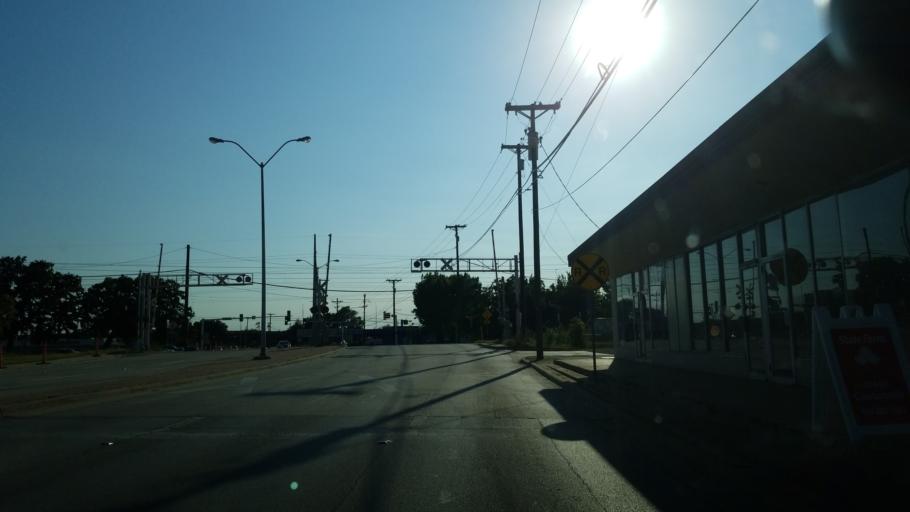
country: US
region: Texas
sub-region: Dallas County
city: Farmers Branch
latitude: 32.9240
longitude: -96.8962
